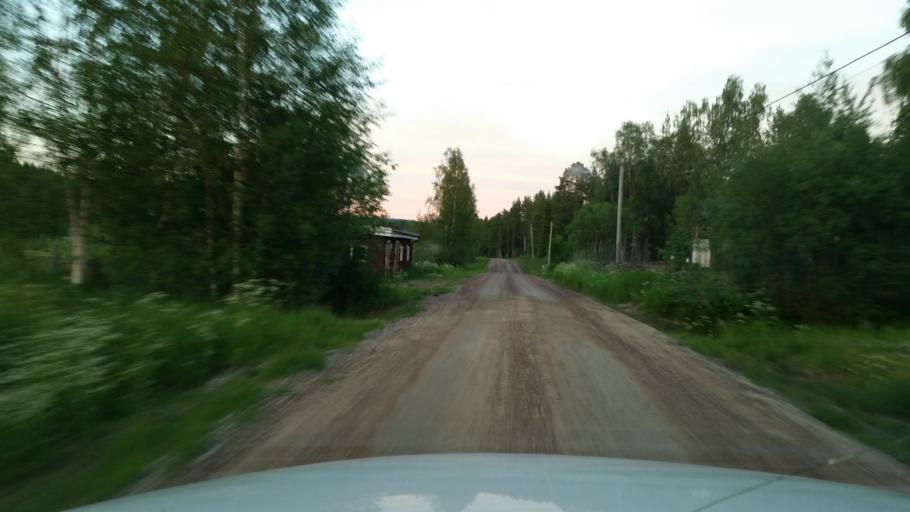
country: SE
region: Vaesternorrland
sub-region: Ange Kommun
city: Ange
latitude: 62.1857
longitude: 15.6289
